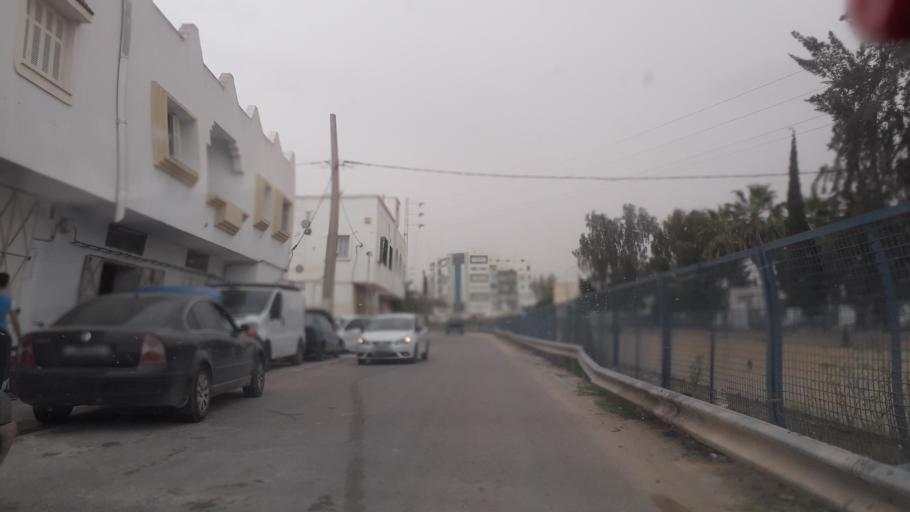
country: TN
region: Safaqis
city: Al Qarmadah
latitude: 34.7976
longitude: 10.7719
